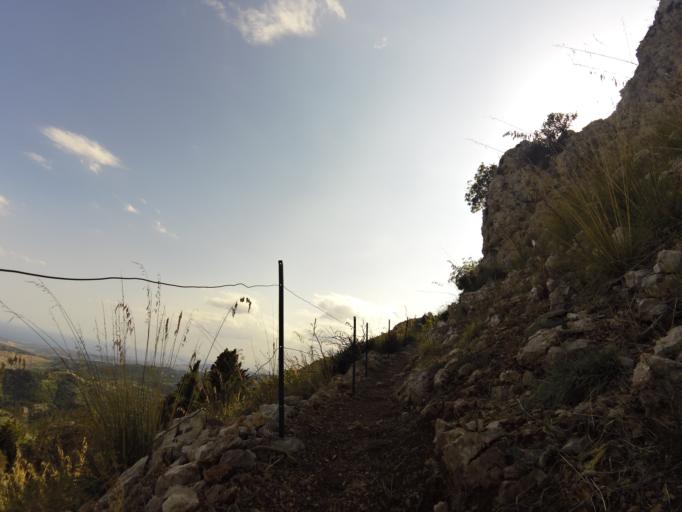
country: IT
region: Calabria
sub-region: Provincia di Reggio Calabria
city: Pazzano
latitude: 38.4708
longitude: 16.4525
